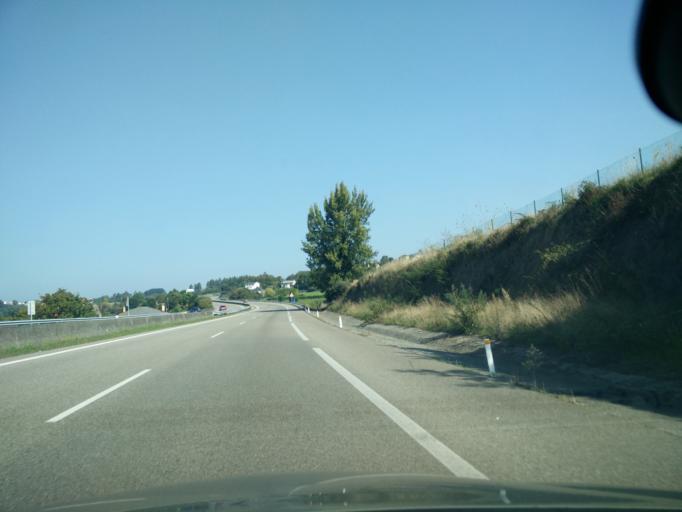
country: ES
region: Galicia
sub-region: Provincia da Coruna
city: Mino
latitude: 43.3562
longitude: -8.2025
